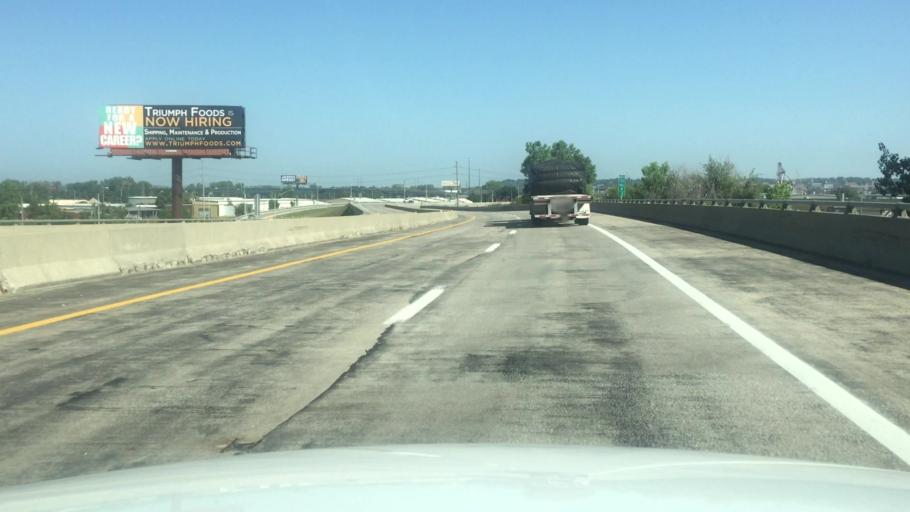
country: US
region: Kansas
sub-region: Doniphan County
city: Elwood
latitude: 39.7389
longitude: -94.8513
